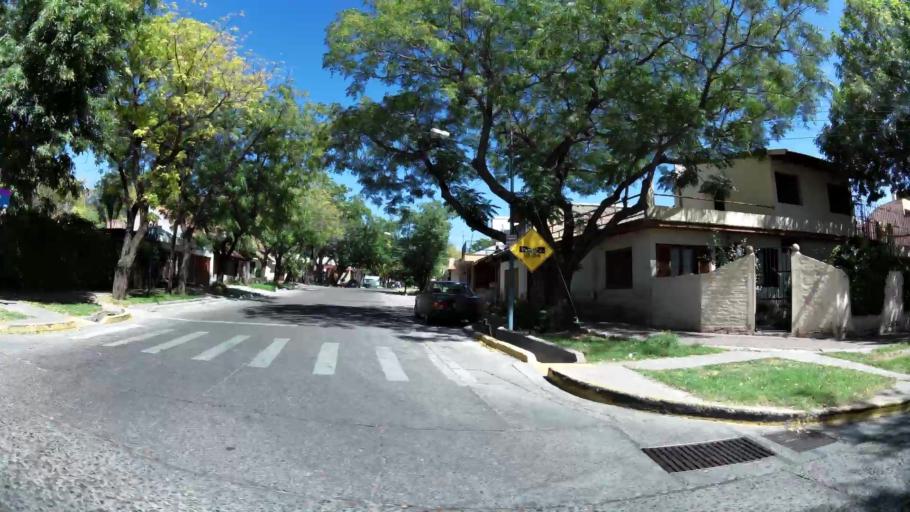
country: AR
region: Mendoza
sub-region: Departamento de Godoy Cruz
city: Godoy Cruz
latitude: -32.9411
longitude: -68.8581
